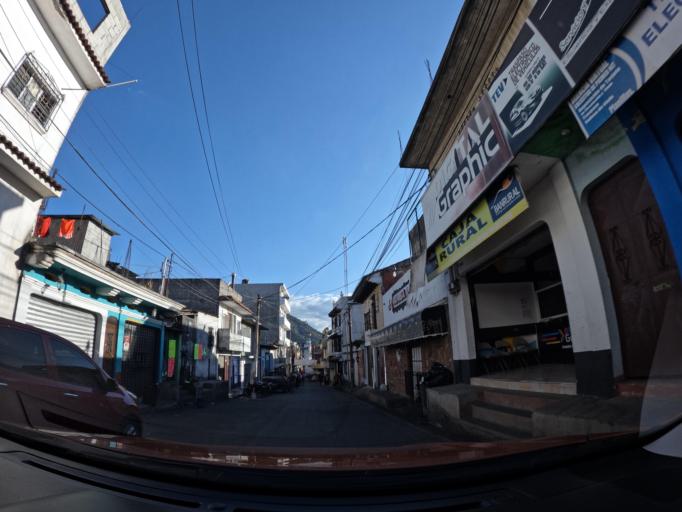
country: GT
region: Escuintla
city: Palin
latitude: 14.4053
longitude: -90.6983
